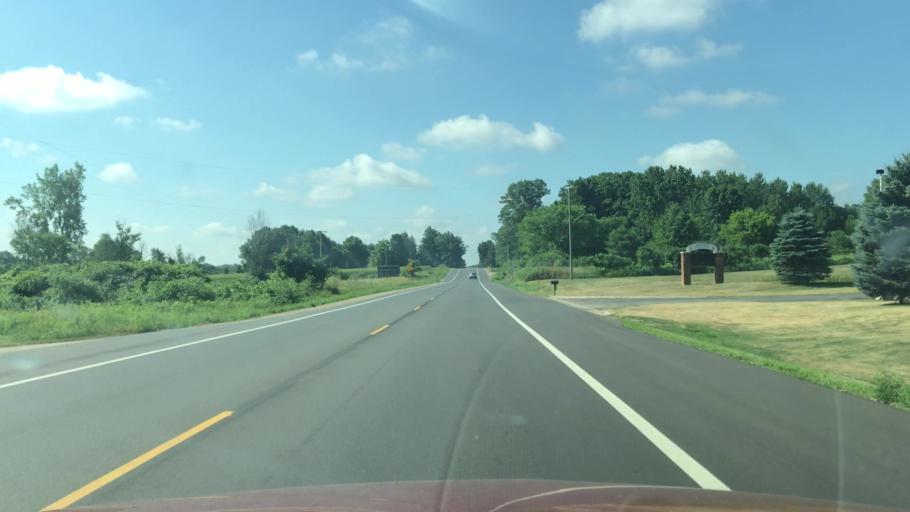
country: US
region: Michigan
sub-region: Newaygo County
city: Newaygo
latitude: 43.3754
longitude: -85.8009
